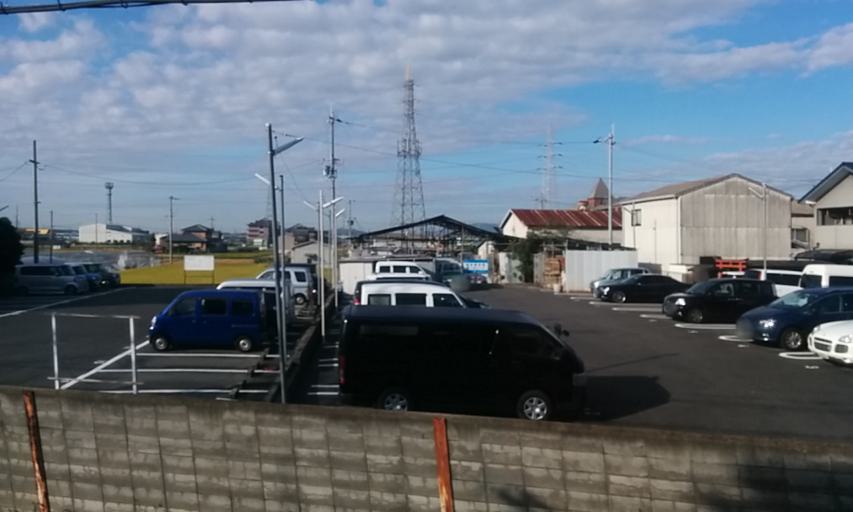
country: JP
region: Kyoto
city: Uji
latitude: 34.9184
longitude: 135.7680
